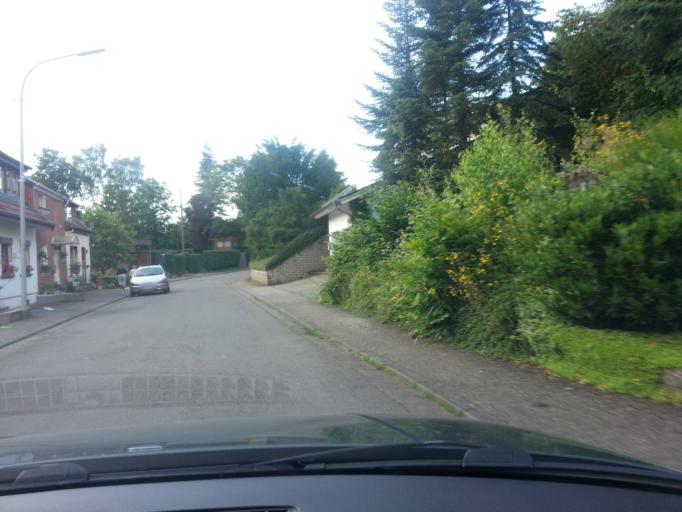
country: DE
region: Saarland
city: Marpingen
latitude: 49.4209
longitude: 7.0774
